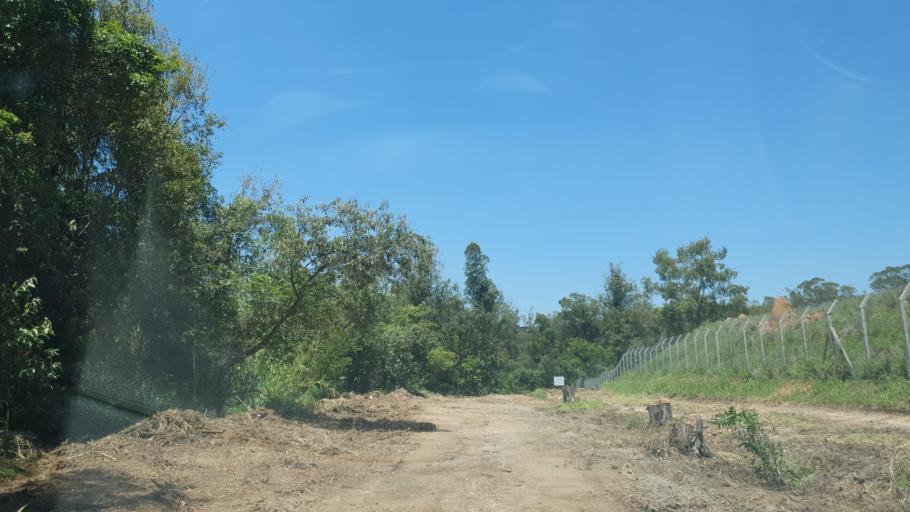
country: BR
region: Sao Paulo
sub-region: Sorocaba
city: Sorocaba
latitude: -23.4726
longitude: -47.4122
